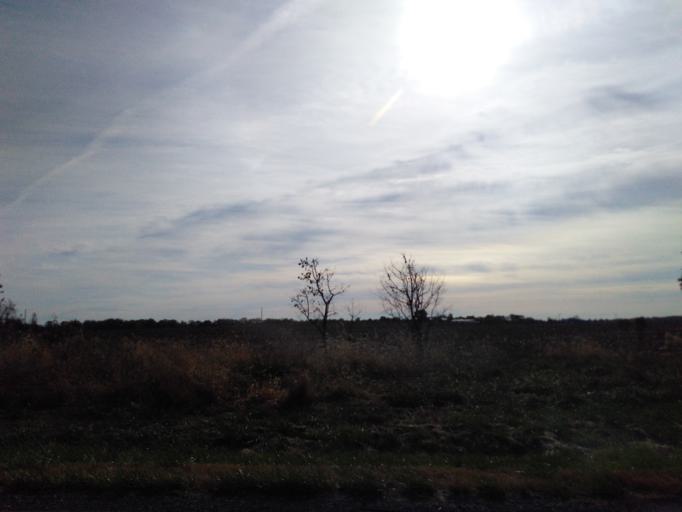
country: US
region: Illinois
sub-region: Madison County
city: Saint Jacob
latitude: 38.7719
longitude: -89.7474
